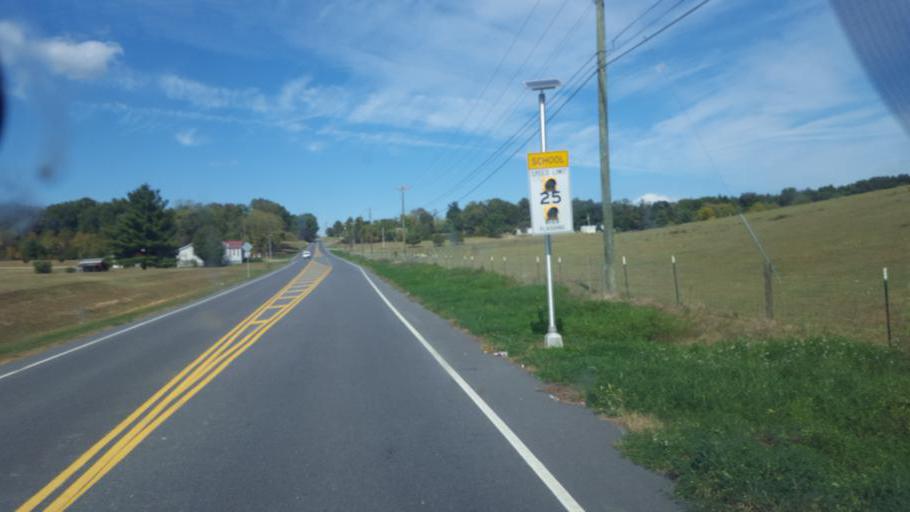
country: US
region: Virginia
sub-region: Page County
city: Luray
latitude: 38.6533
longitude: -78.4826
